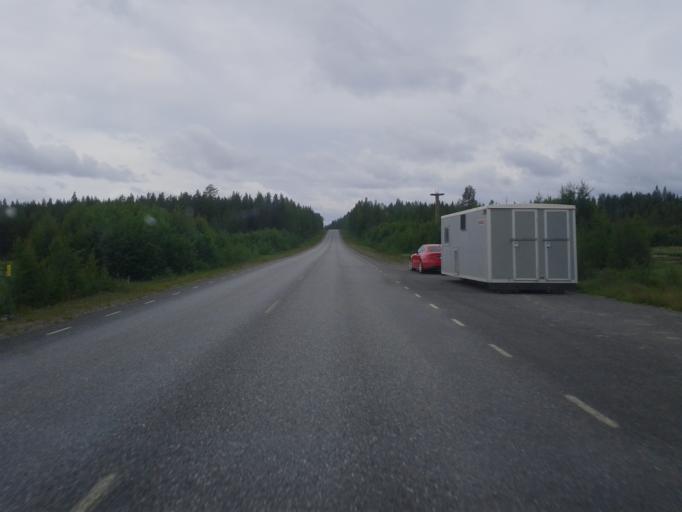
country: SE
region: Vaesterbotten
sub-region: Skelleftea Kommun
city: Langsele
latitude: 64.8852
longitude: 20.2886
